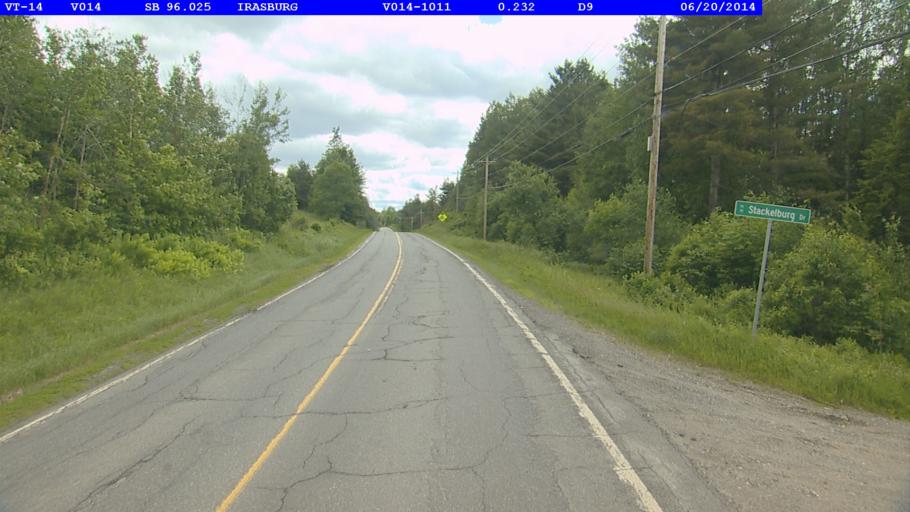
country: US
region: Vermont
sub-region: Orleans County
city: Newport
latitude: 44.7790
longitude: -72.3139
